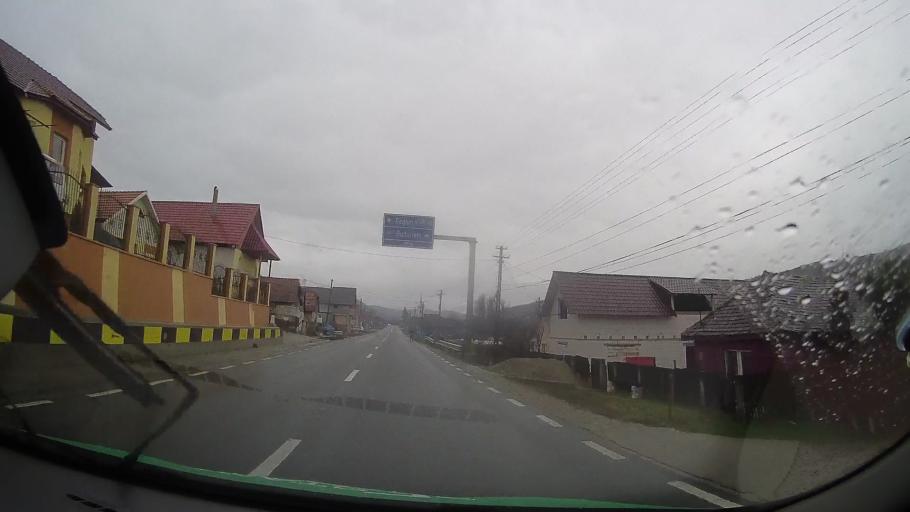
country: RO
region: Bistrita-Nasaud
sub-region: Comuna Galatii Bistritei
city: Galatii Bistritei
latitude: 46.9491
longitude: 24.4527
